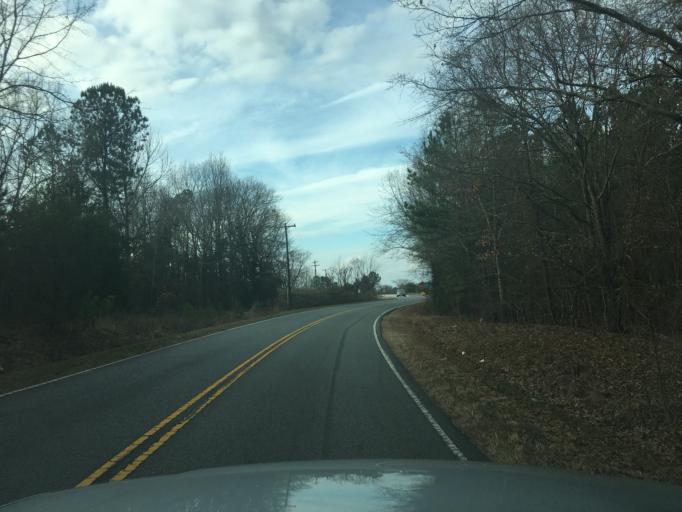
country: US
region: South Carolina
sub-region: Abbeville County
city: Lake Secession
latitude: 34.3615
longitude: -82.5191
